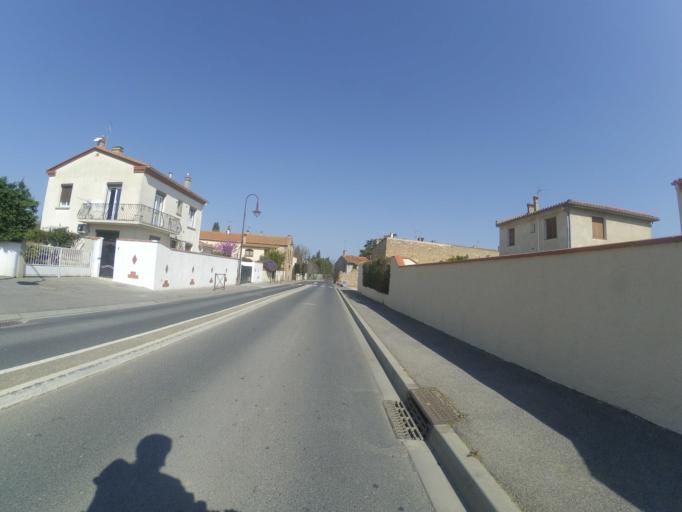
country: FR
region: Languedoc-Roussillon
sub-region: Departement des Pyrenees-Orientales
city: Llupia
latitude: 42.6191
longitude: 2.7685
